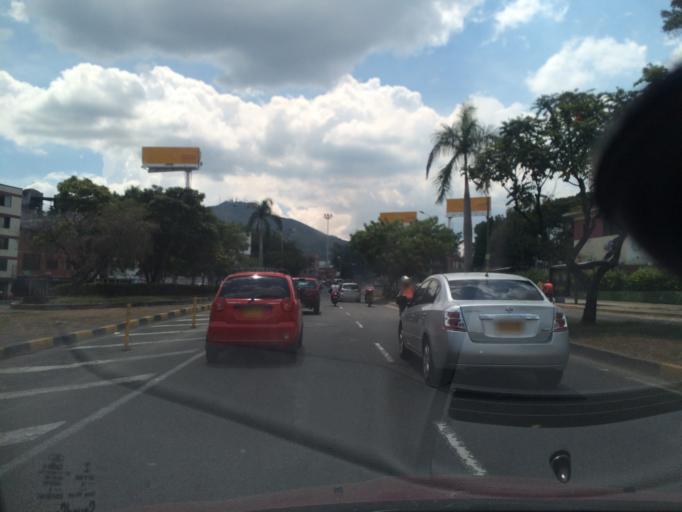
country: CO
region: Valle del Cauca
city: Cali
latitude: 3.4410
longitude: -76.5364
